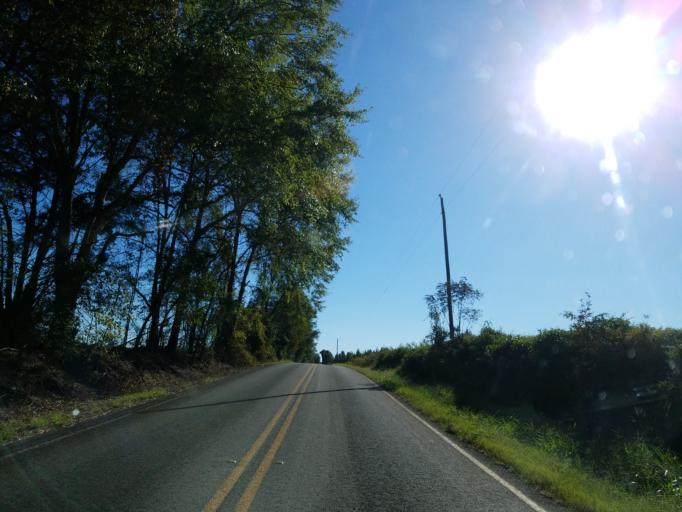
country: US
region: Georgia
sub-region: Dooly County
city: Vienna
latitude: 32.2145
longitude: -83.8934
